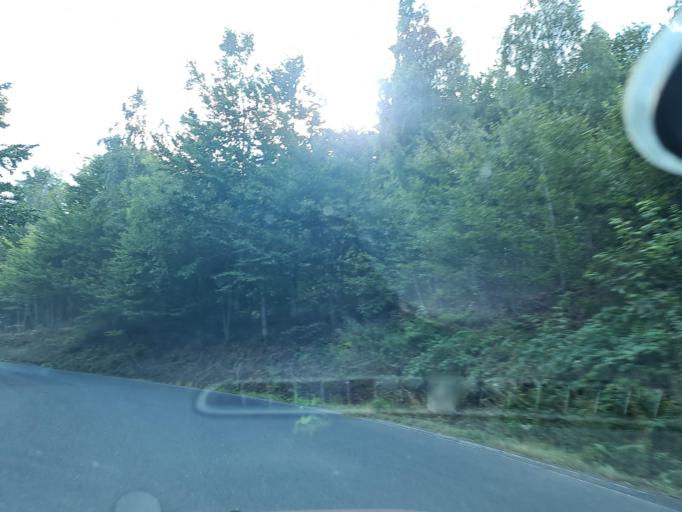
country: CZ
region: Ustecky
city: Mezibori
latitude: 50.6194
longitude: 13.5791
